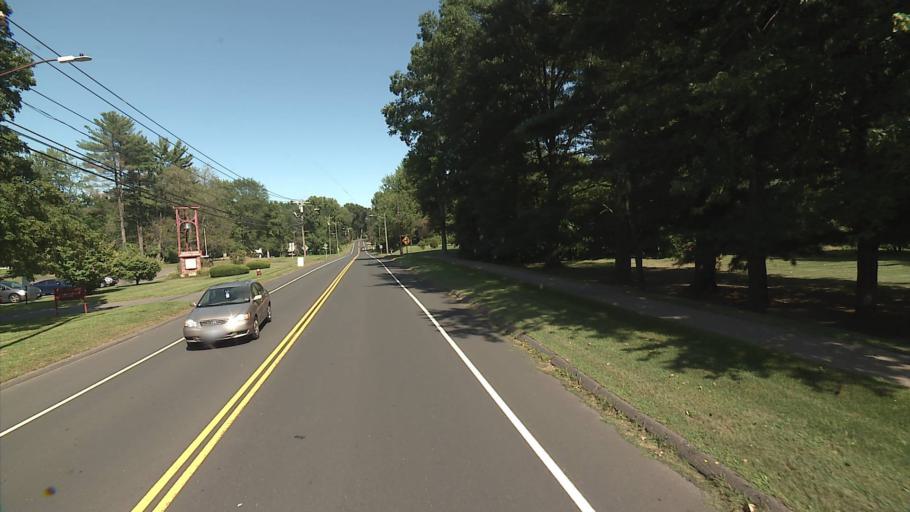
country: US
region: Connecticut
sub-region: Hartford County
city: Windsor
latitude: 41.8386
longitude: -72.6621
